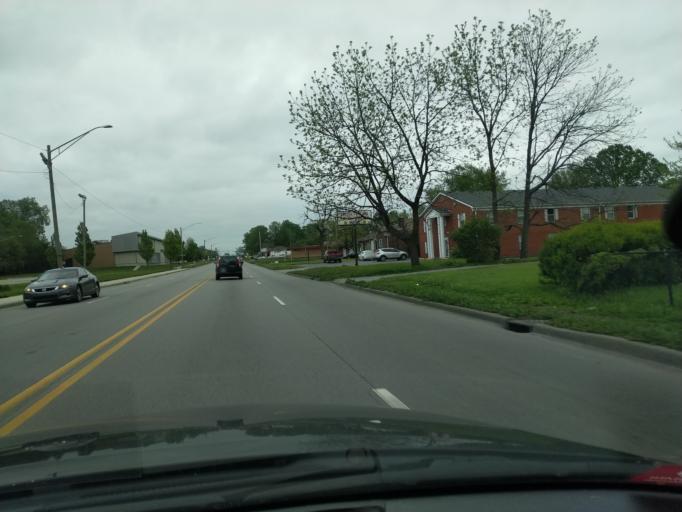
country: US
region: Indiana
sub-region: Marion County
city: Warren Park
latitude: 39.8254
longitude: -86.0782
